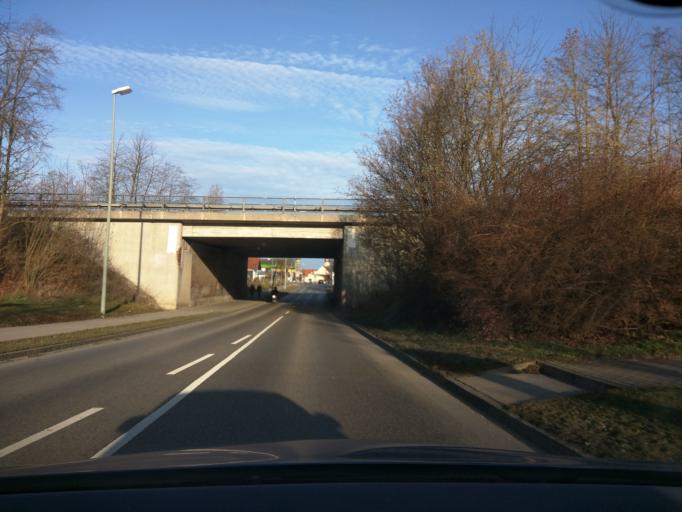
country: DE
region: Bavaria
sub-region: Upper Bavaria
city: Wolnzach
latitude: 48.5956
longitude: 11.6316
